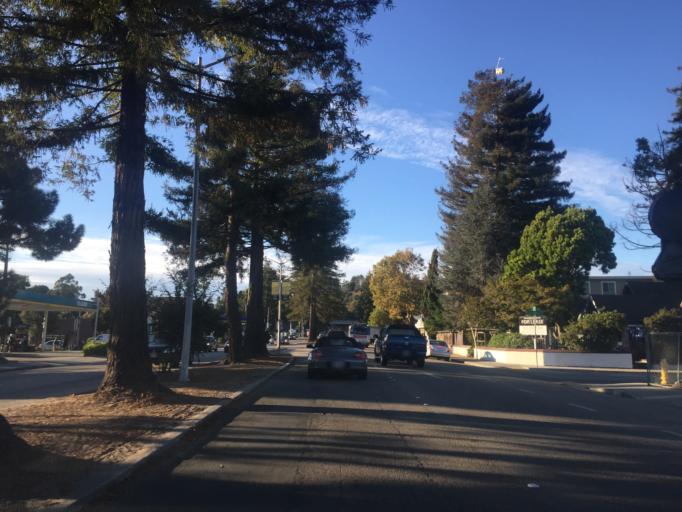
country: US
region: California
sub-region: Santa Cruz County
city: Santa Cruz
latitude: 36.9832
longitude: -122.0226
